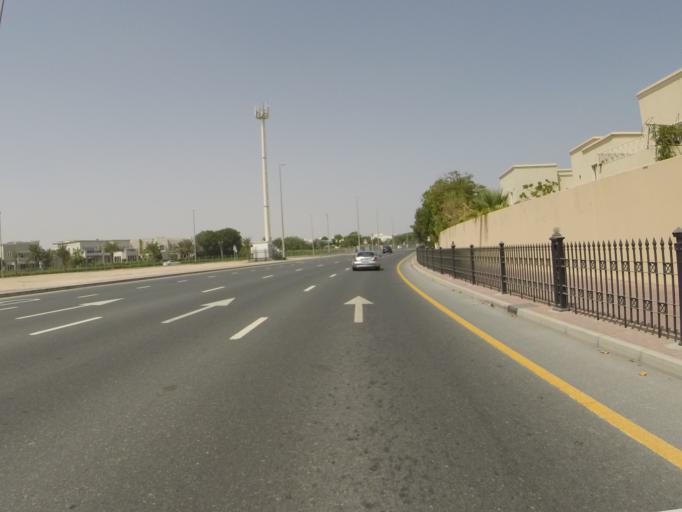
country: AE
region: Dubai
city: Dubai
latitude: 25.0774
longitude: 55.1772
